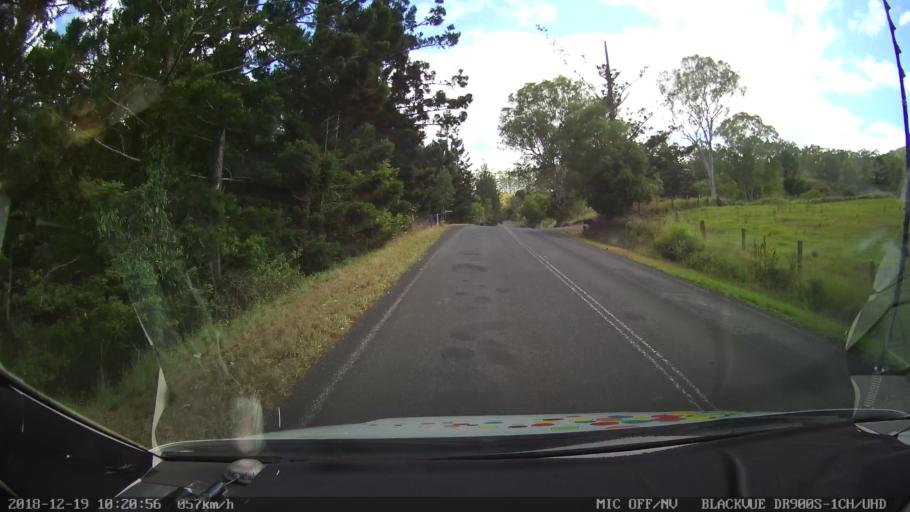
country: AU
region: New South Wales
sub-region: Kyogle
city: Kyogle
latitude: -28.6019
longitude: 153.0573
